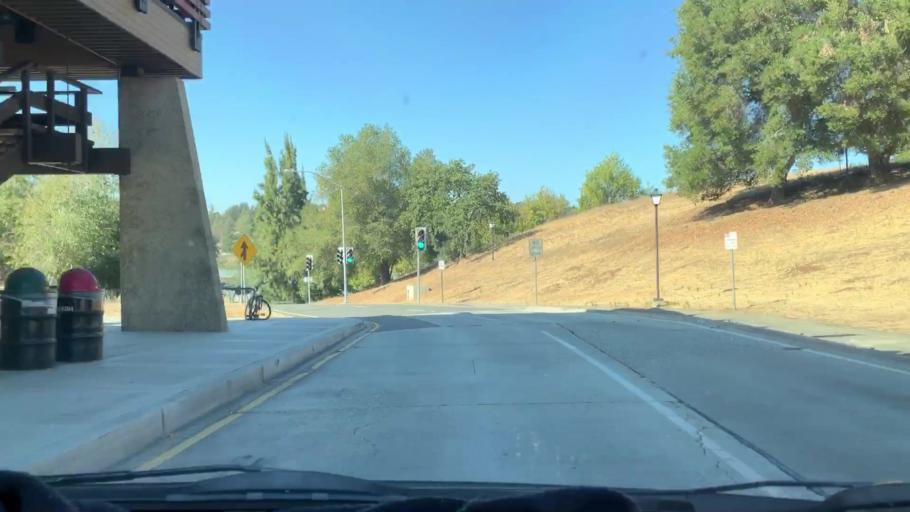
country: US
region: California
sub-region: Santa Clara County
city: Los Altos Hills
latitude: 37.3626
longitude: -122.1267
